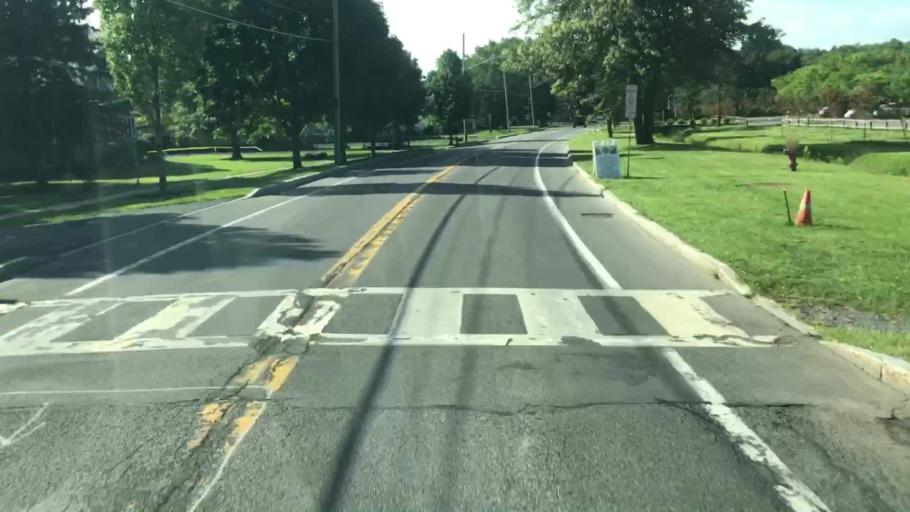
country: US
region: New York
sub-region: Onondaga County
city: Skaneateles
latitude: 42.9542
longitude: -76.4256
